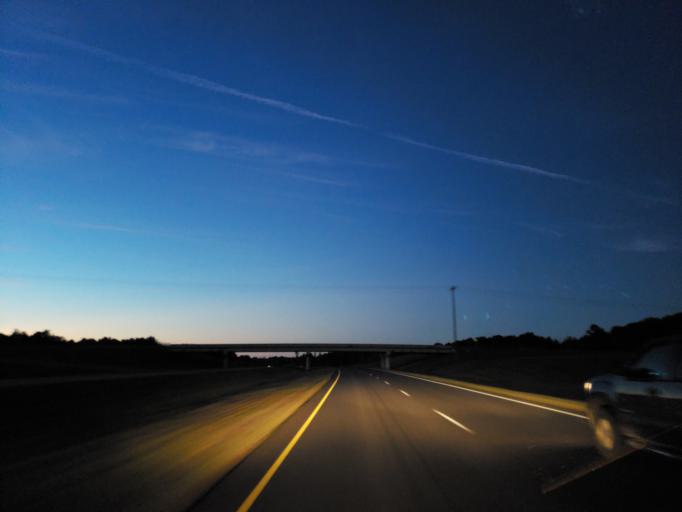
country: US
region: Mississippi
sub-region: Clarke County
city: Quitman
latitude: 32.0578
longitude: -88.6777
